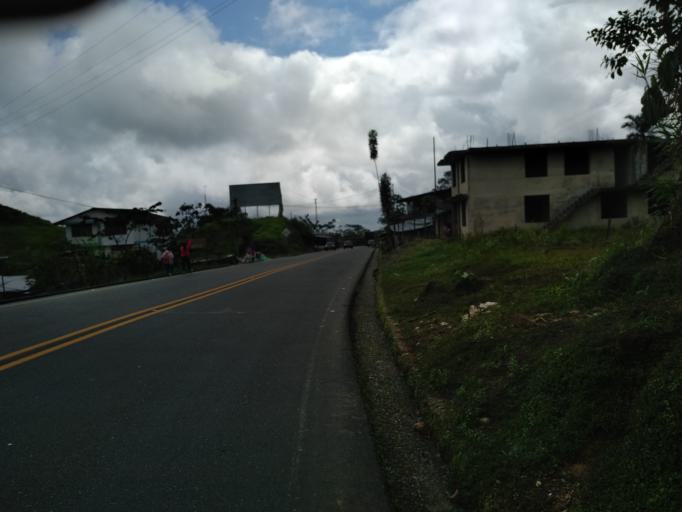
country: CO
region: Narino
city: Ricaurte
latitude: 1.3617
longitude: -78.1843
